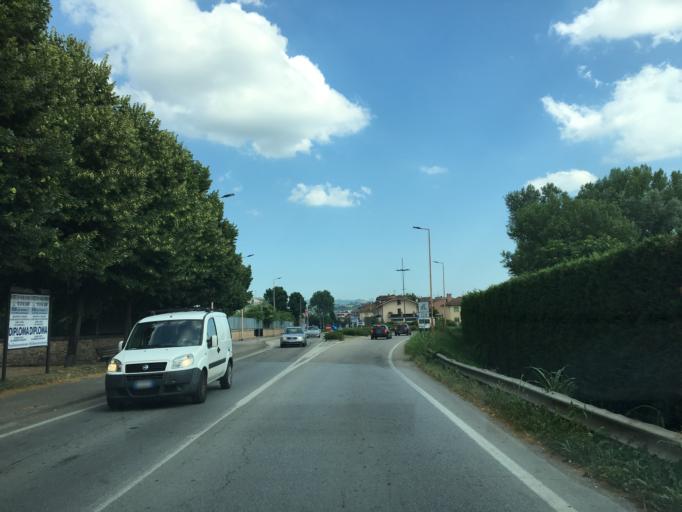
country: IT
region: Piedmont
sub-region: Provincia di Cuneo
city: Mussotto
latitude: 44.7159
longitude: 8.0127
